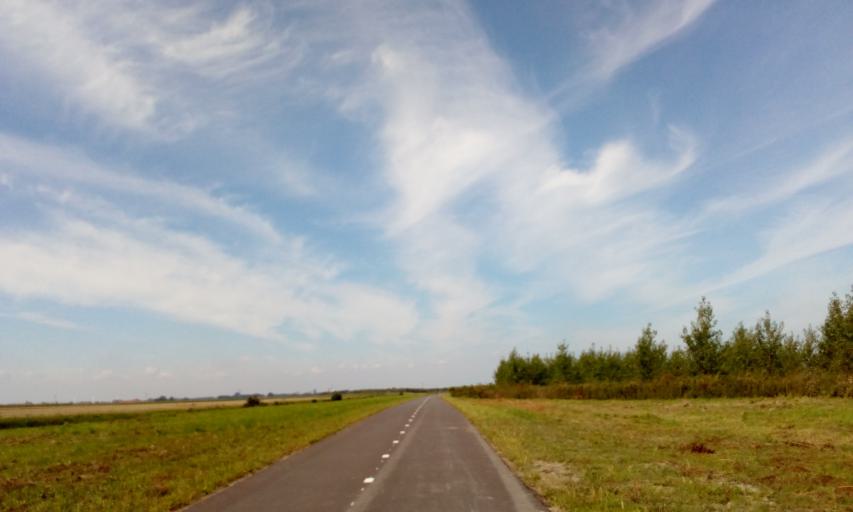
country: NL
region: South Holland
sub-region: Gemeente Waddinxveen
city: Groenswaard
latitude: 52.0657
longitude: 4.6200
